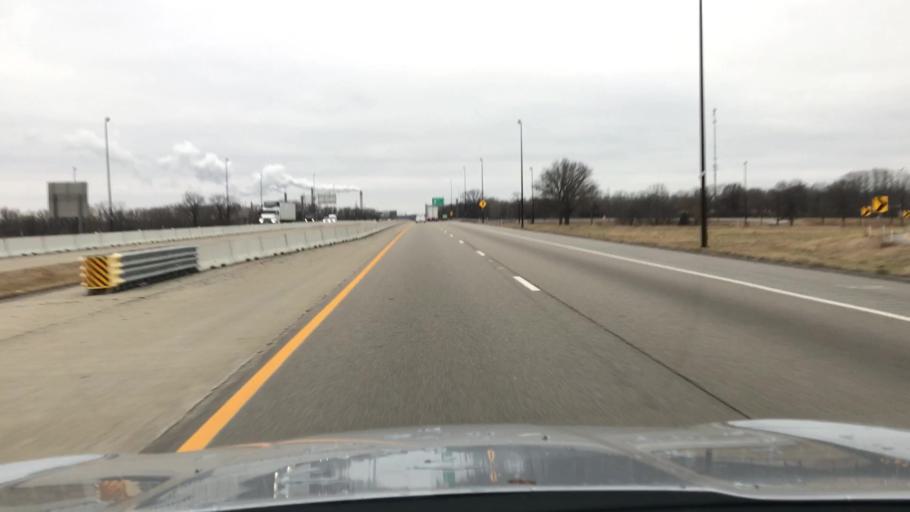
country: US
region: Illinois
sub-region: Sangamon County
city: Grandview
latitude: 39.7891
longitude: -89.5988
